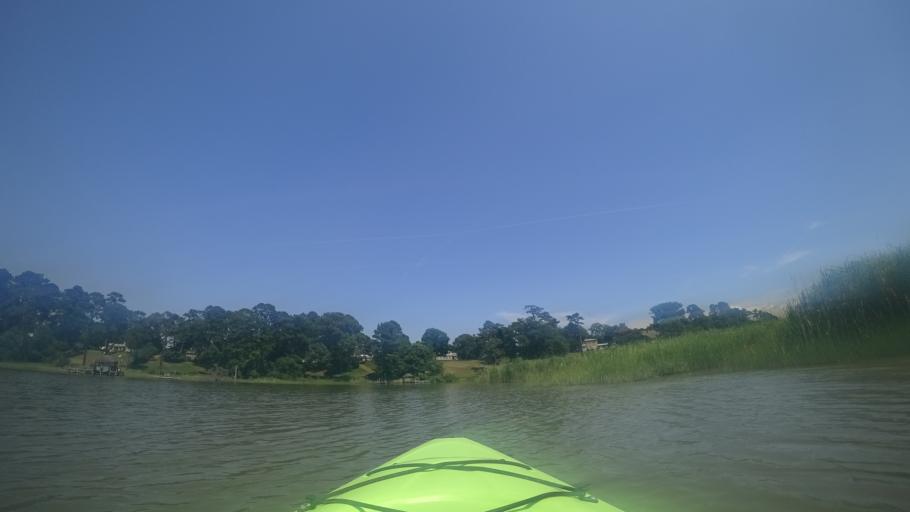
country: US
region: Virginia
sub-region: Isle of Wight County
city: Smithfield
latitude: 36.9747
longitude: -76.6168
